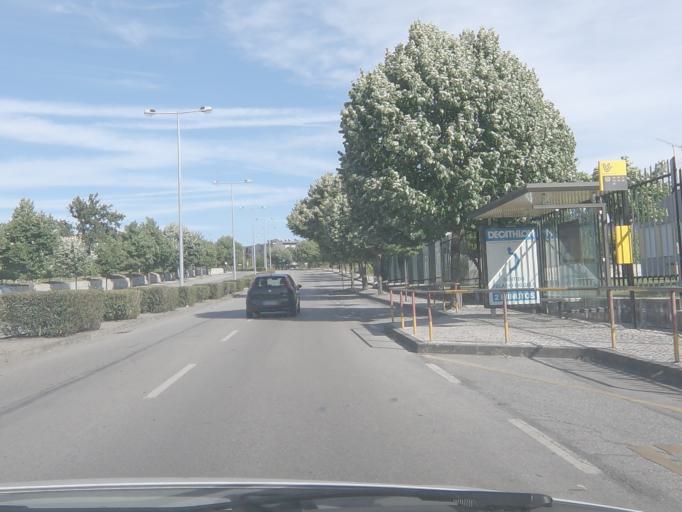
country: PT
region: Viseu
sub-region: Viseu
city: Viseu
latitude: 40.6425
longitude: -7.9204
